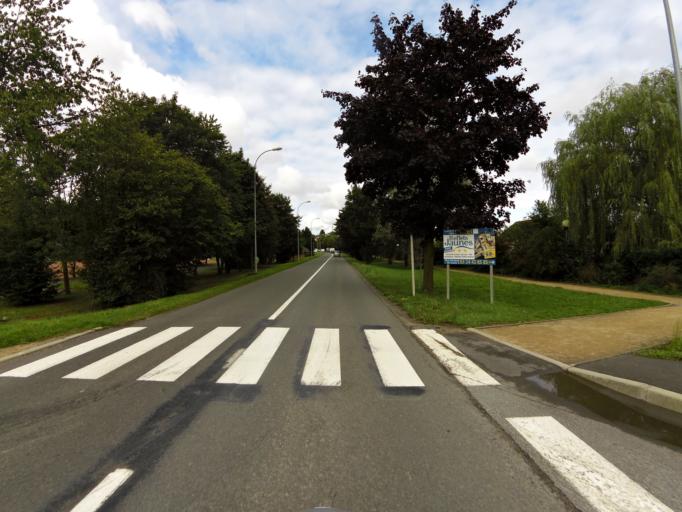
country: FR
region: Champagne-Ardenne
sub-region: Departement des Ardennes
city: Fromelennes
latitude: 50.1342
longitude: 4.8476
